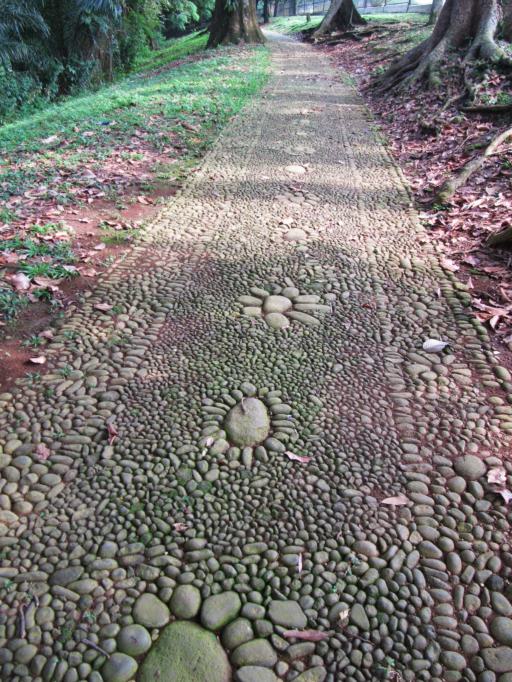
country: ID
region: West Java
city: Bogor
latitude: -6.5963
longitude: 106.7992
